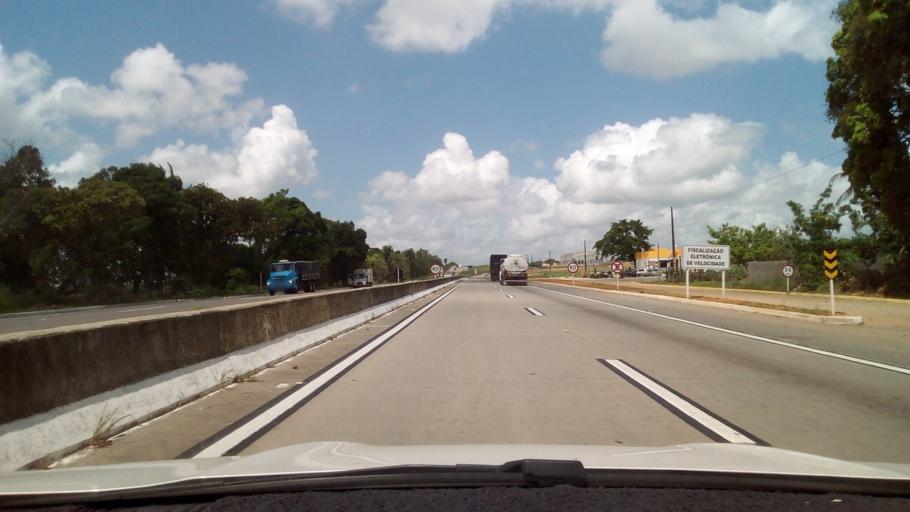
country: BR
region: Paraiba
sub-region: Alhandra
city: Alhandra
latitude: -7.3645
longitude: -34.9526
